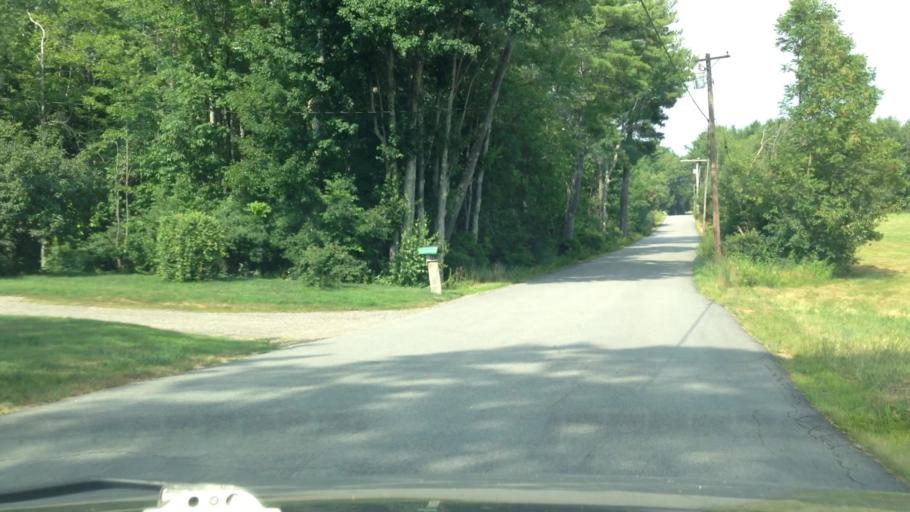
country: US
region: New Hampshire
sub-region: Cheshire County
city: Marlborough
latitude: 42.8796
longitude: -72.2017
